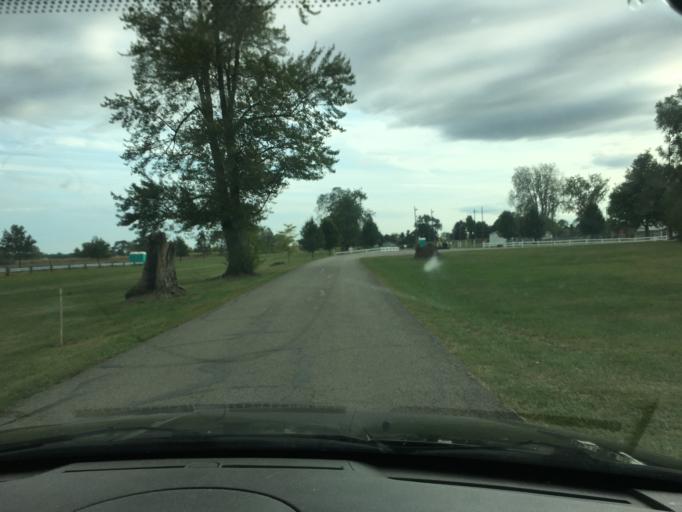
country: US
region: Ohio
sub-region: Logan County
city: West Liberty
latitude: 40.2563
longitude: -83.7447
